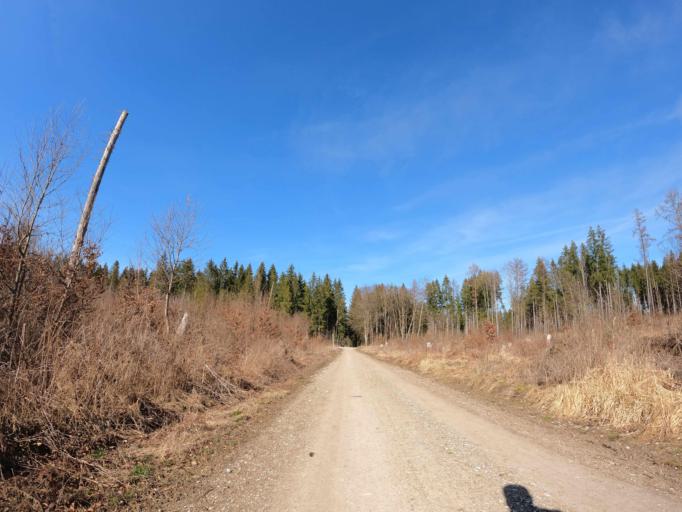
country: DE
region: Bavaria
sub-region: Upper Bavaria
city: Sauerlach
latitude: 48.0010
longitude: 11.6331
